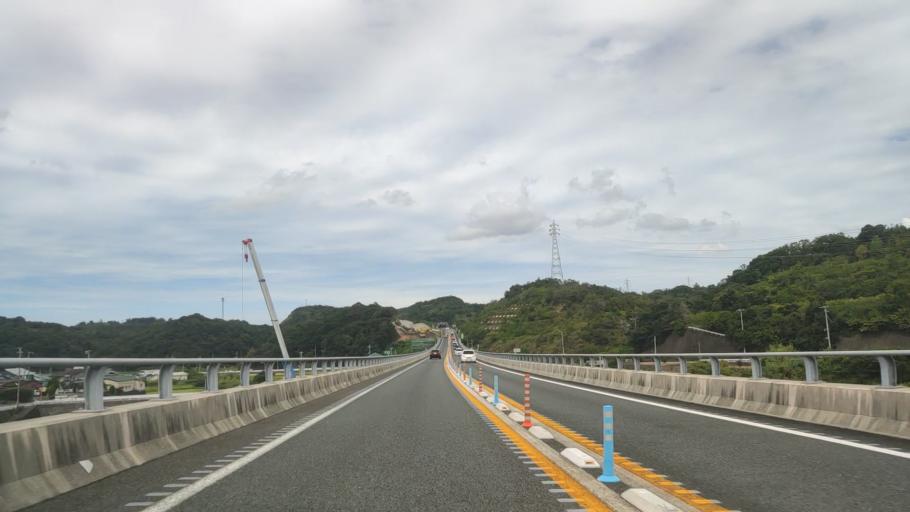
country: JP
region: Wakayama
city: Gobo
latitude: 33.8681
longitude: 135.1899
